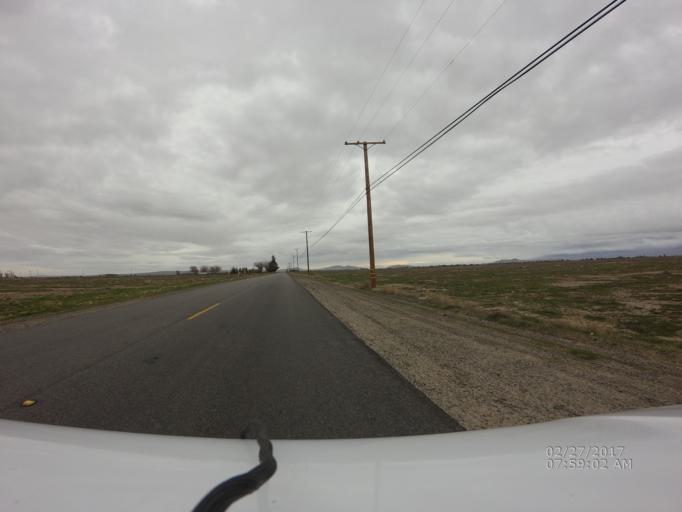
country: US
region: California
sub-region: Los Angeles County
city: Lancaster
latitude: 34.7048
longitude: -117.9916
